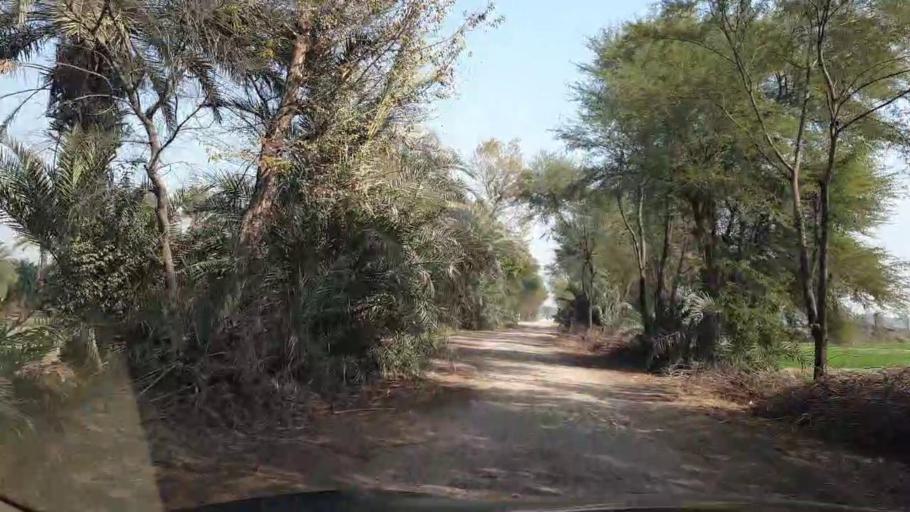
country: PK
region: Sindh
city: Ubauro
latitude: 28.1132
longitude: 69.7765
